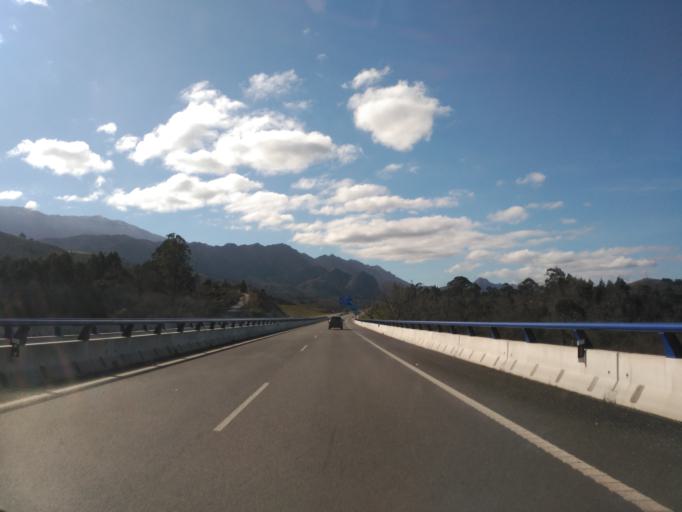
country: ES
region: Asturias
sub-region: Province of Asturias
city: Llanes
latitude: 43.4013
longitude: -4.6980
